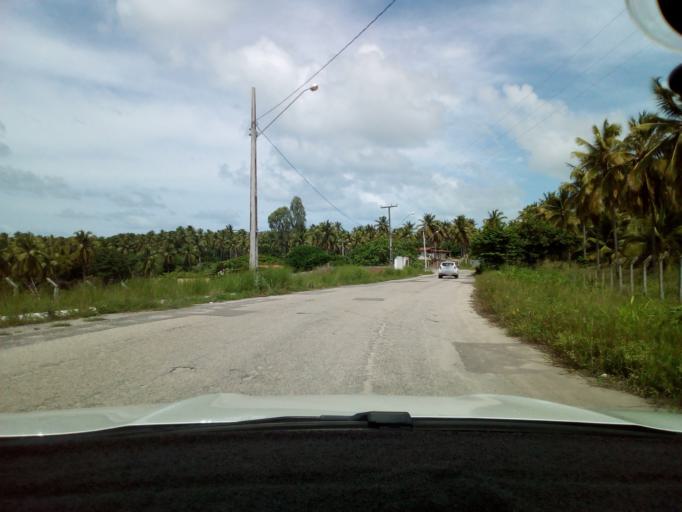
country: BR
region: Paraiba
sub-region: Joao Pessoa
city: Joao Pessoa
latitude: -7.1993
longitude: -34.8072
